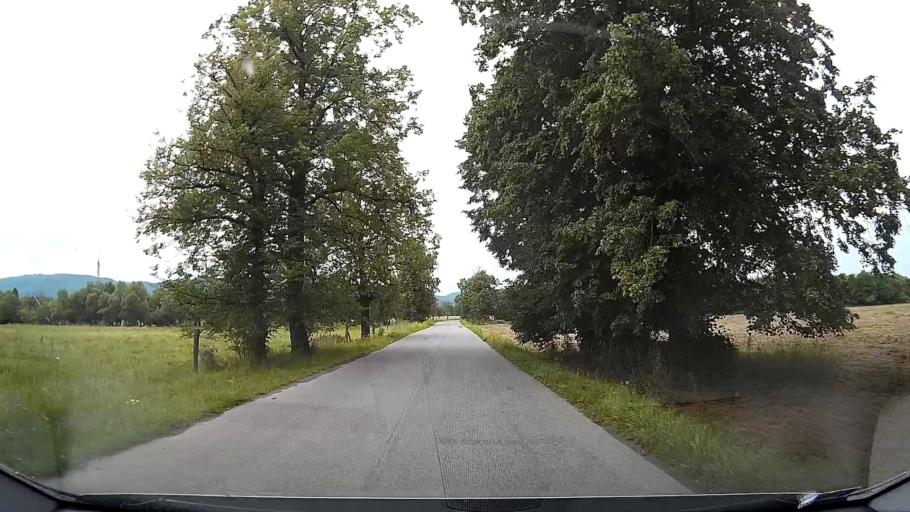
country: SK
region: Presovsky
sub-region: Okres Poprad
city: Poprad
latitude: 48.9874
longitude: 20.3796
